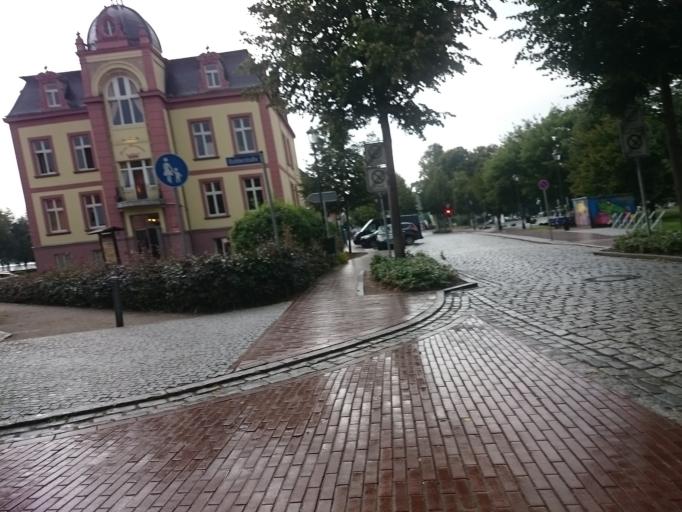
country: DE
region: Mecklenburg-Vorpommern
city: Waren
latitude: 53.5142
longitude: 12.6845
